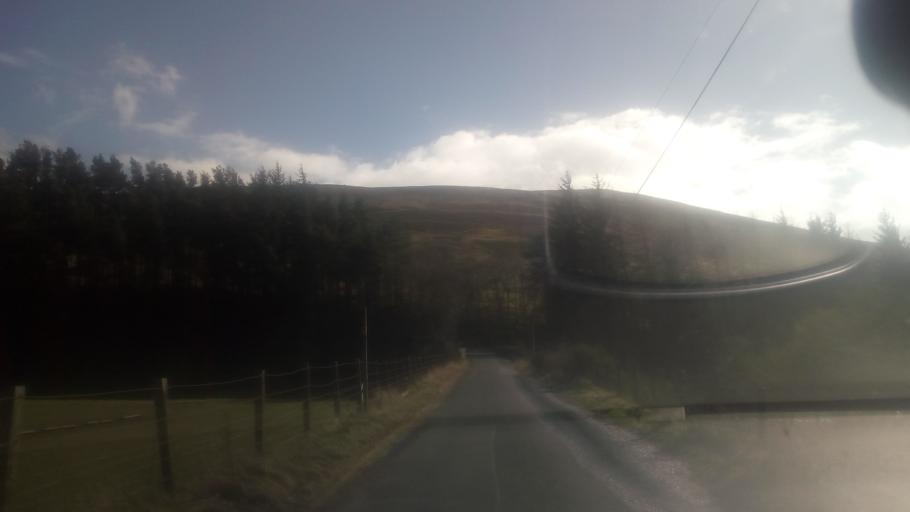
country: GB
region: Scotland
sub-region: The Scottish Borders
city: Innerleithen
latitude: 55.5121
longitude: -3.0969
